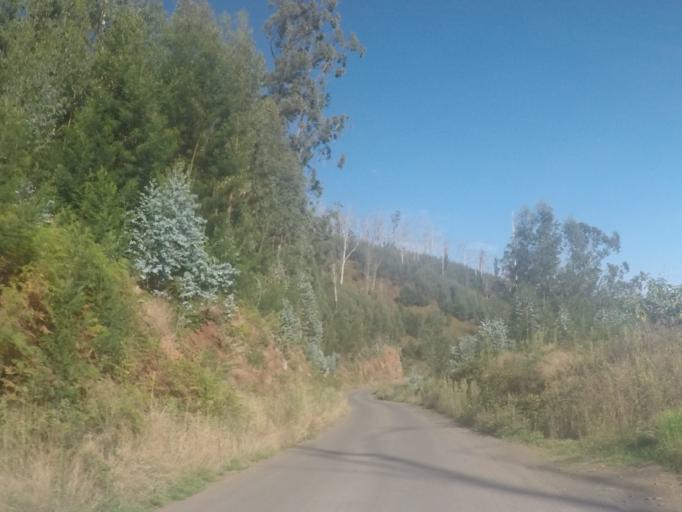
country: PT
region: Madeira
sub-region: Funchal
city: Nossa Senhora do Monte
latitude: 32.6901
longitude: -16.9056
